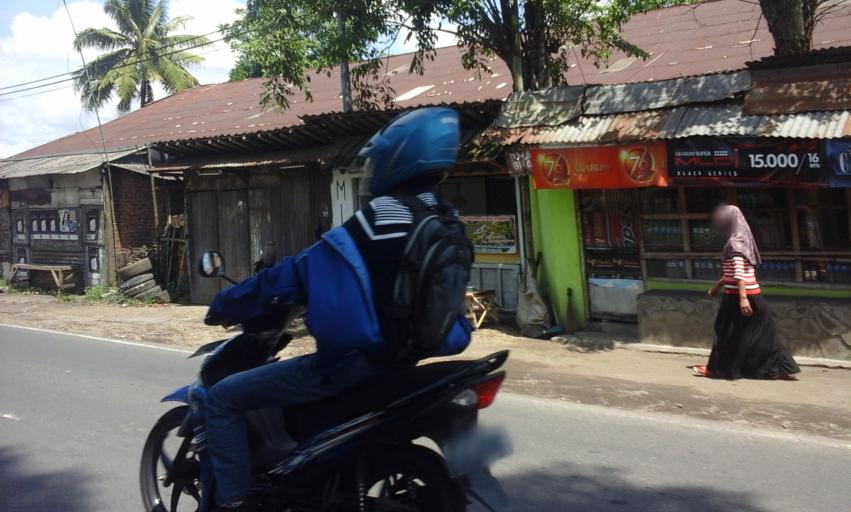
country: ID
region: East Java
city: Kertosari
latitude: -8.1879
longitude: 113.7516
